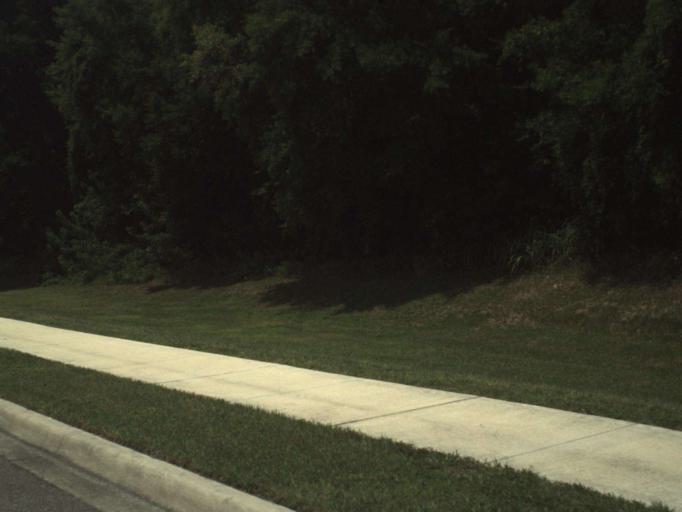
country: US
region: Florida
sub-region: Seminole County
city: Forest City
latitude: 28.6497
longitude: -81.4155
